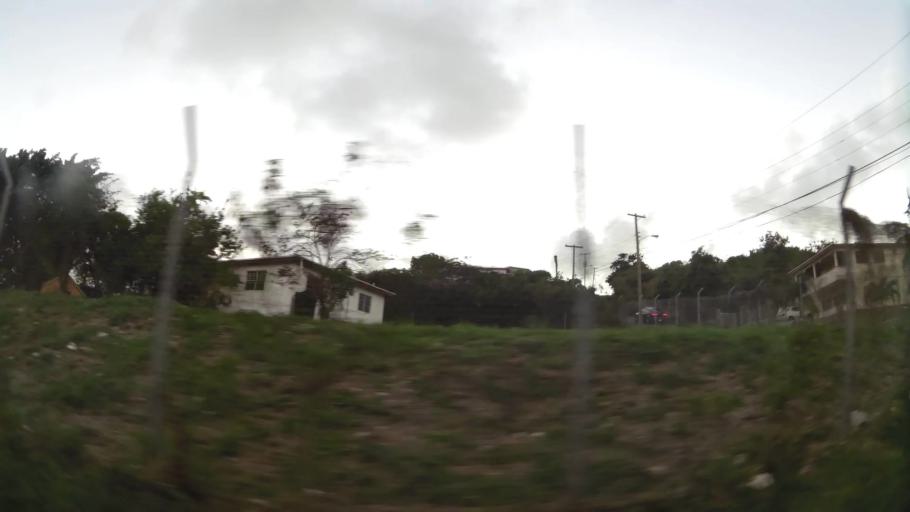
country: AG
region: Saint George
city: Piggotts
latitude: 17.1346
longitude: -61.8022
